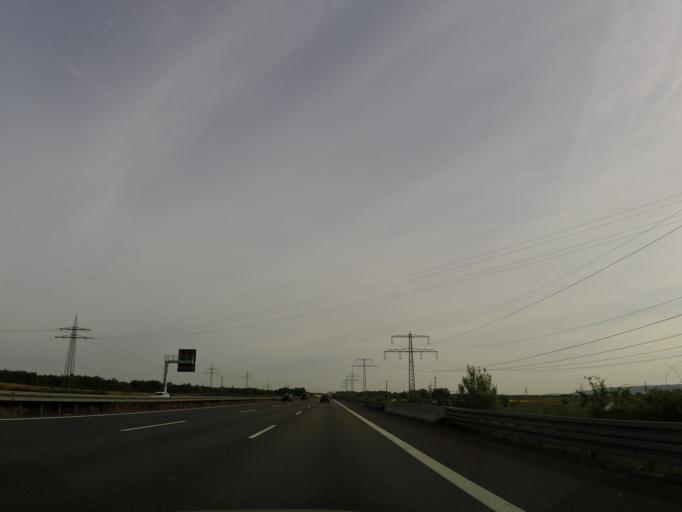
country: DE
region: Lower Saxony
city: Rosdorf
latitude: 51.5058
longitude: 9.8783
